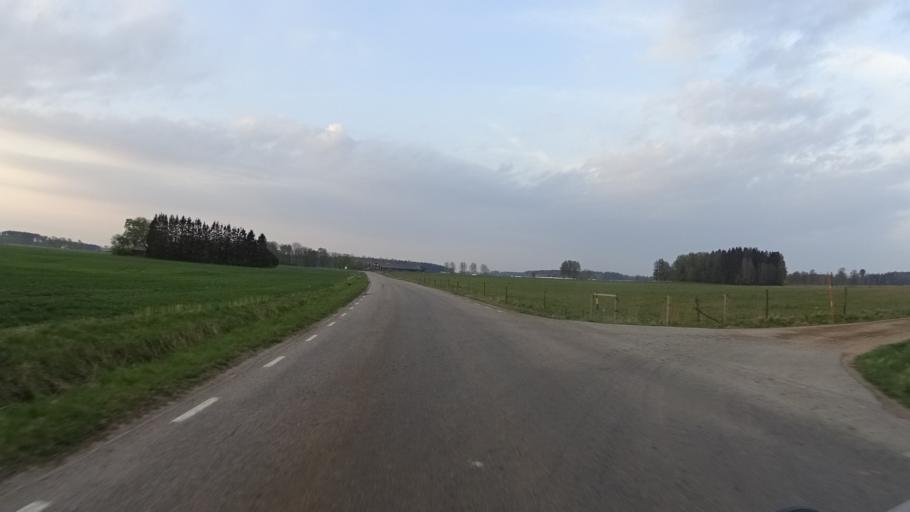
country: SE
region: Vaestra Goetaland
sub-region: Gotene Kommun
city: Kallby
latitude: 58.4700
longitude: 13.3295
